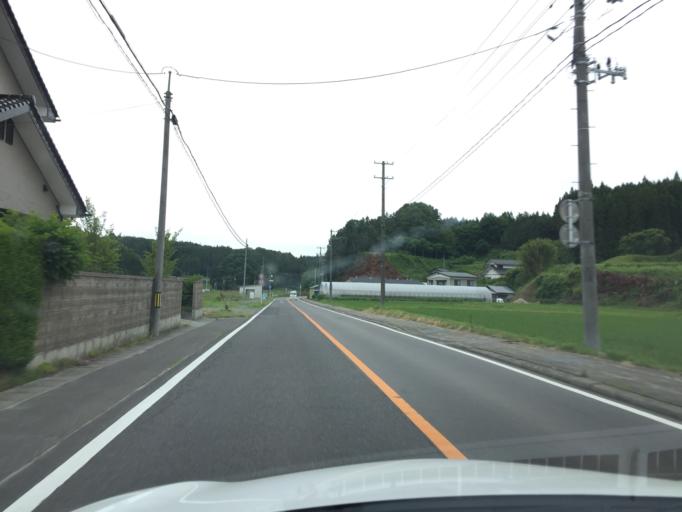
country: JP
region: Fukushima
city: Funehikimachi-funehiki
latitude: 37.3120
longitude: 140.6582
